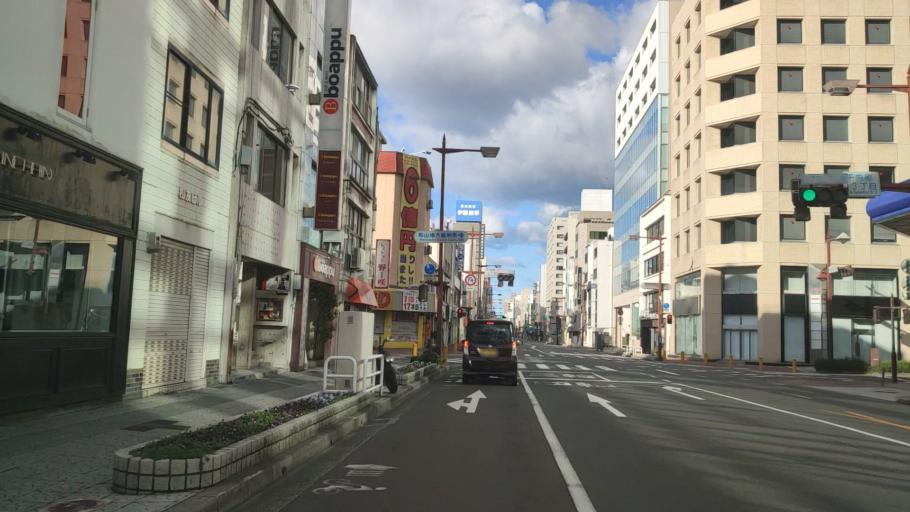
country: JP
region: Ehime
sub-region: Shikoku-chuo Shi
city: Matsuyama
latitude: 33.8367
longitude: 132.7684
